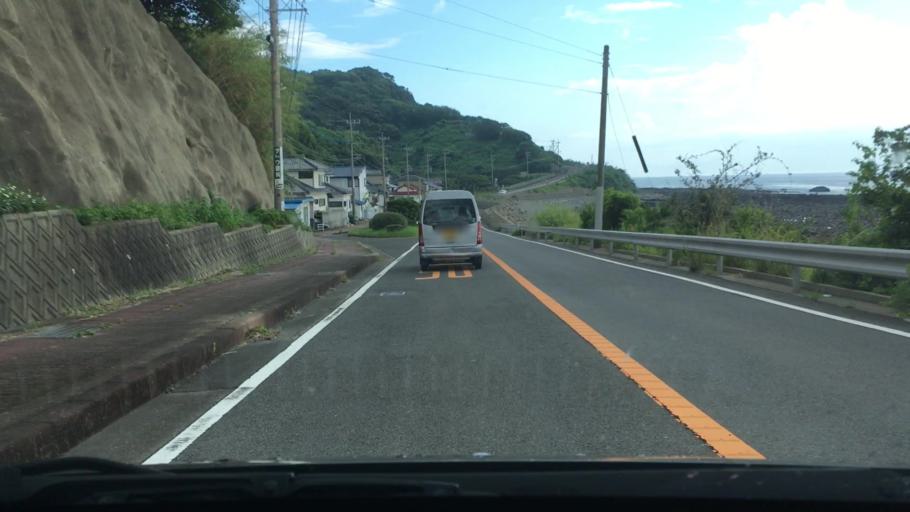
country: JP
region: Nagasaki
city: Togitsu
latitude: 32.8770
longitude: 129.6798
